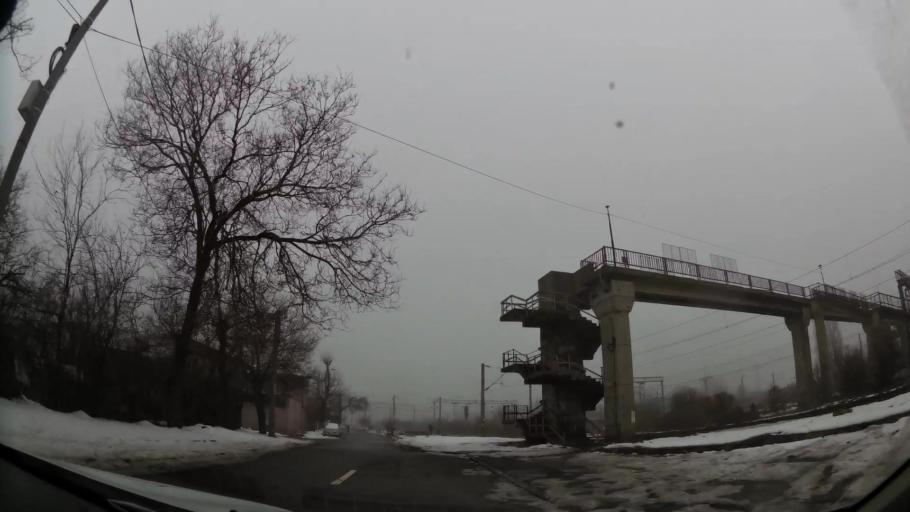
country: RO
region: Ilfov
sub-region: Comuna Chiajna
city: Rosu
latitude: 44.4681
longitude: 26.0407
